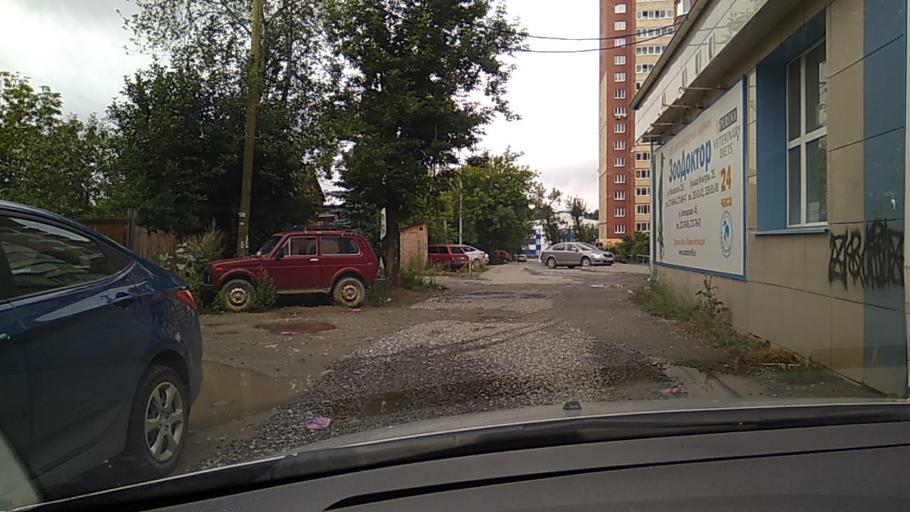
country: RU
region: Sverdlovsk
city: Sovkhoznyy
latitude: 56.7667
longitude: 60.6053
